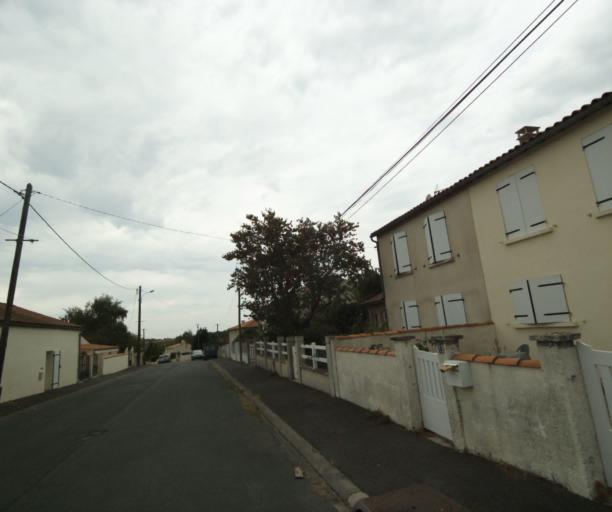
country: FR
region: Poitou-Charentes
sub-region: Departement de la Charente-Maritime
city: Tonnay-Charente
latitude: 45.9469
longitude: -0.8847
